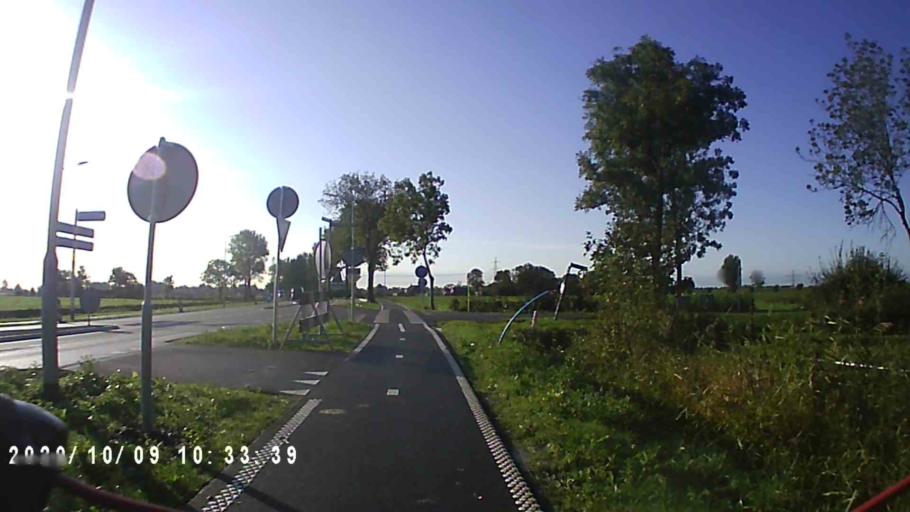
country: NL
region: Groningen
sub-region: Gemeente Winsum
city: Winsum
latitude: 53.3042
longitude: 6.5315
